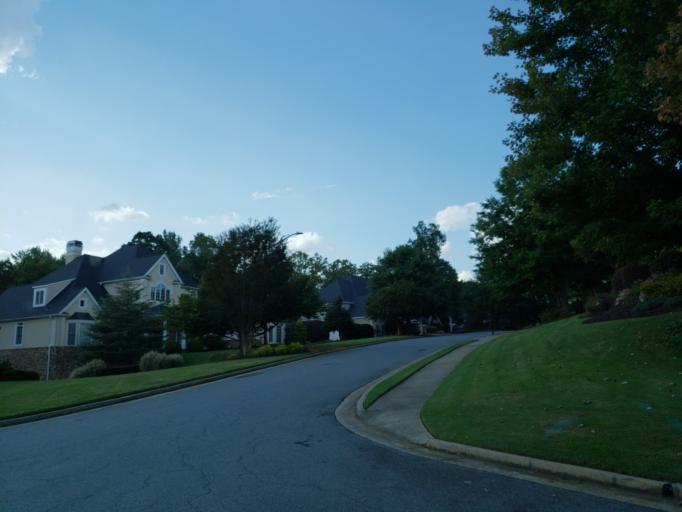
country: US
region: Georgia
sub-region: Cherokee County
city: Woodstock
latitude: 34.0571
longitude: -84.4445
